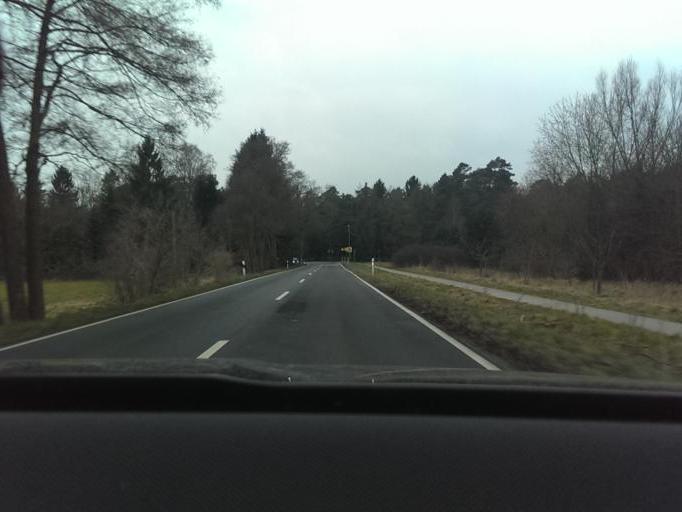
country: DE
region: Lower Saxony
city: Isernhagen Farster Bauerschaft
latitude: 52.5166
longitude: 9.7985
